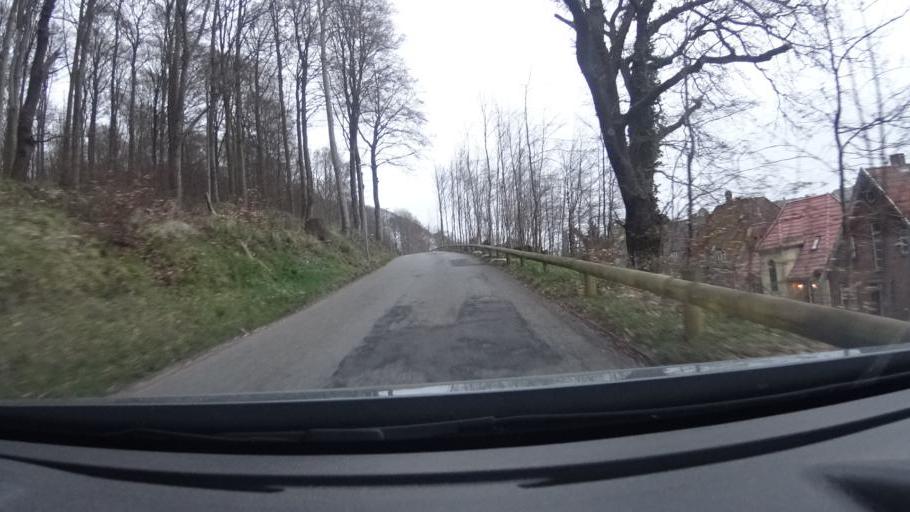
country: DK
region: South Denmark
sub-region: Vejle Kommune
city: Vejle
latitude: 55.7125
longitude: 9.5503
